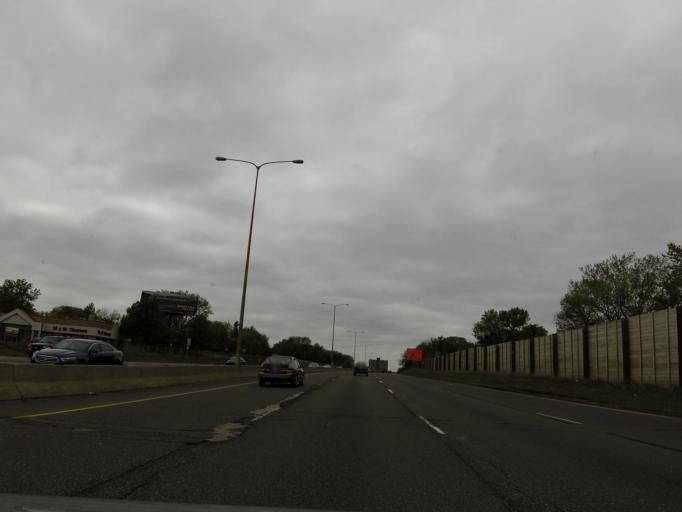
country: US
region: Minnesota
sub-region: Ramsey County
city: Maplewood
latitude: 44.9515
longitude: -93.0283
